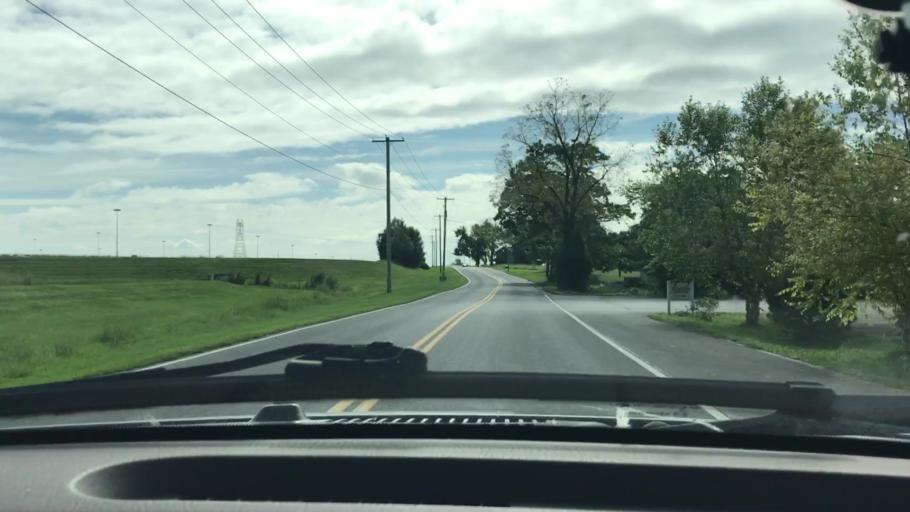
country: US
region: Pennsylvania
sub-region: Lancaster County
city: Manheim
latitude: 40.1412
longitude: -76.4076
